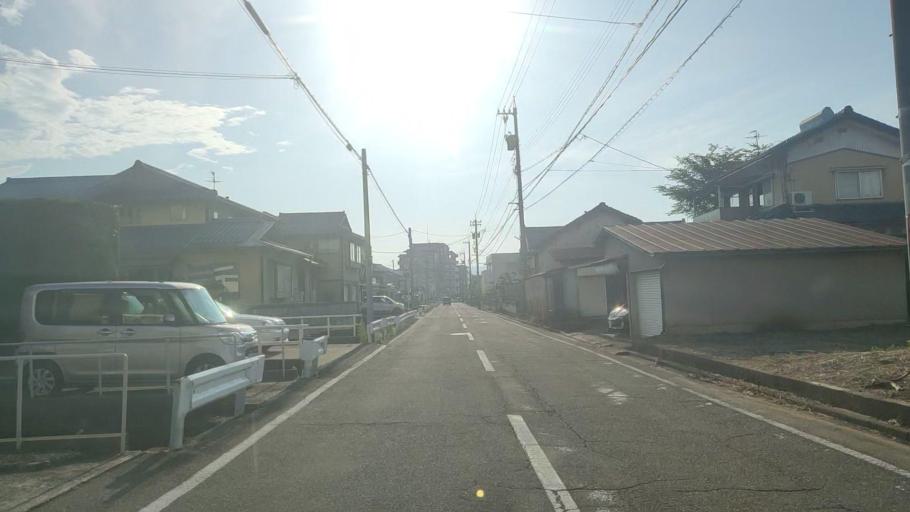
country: JP
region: Fukui
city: Fukui-shi
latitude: 36.0499
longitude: 136.2374
